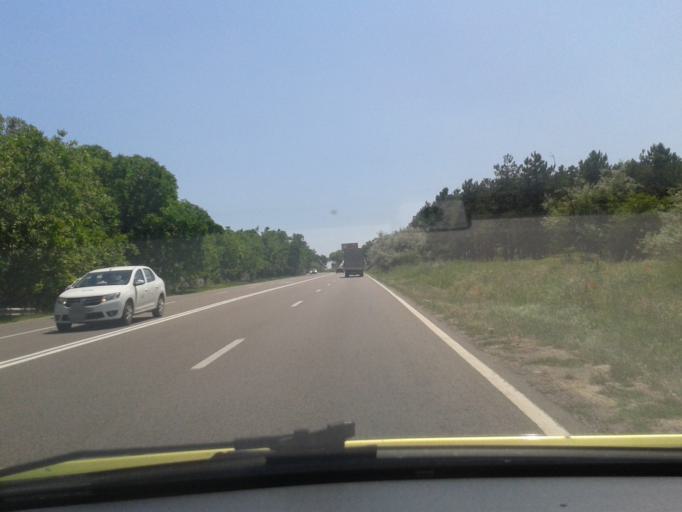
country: RO
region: Constanta
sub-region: Comuna Douazeci si Trei August
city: Douazeci si Trei August
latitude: 43.9012
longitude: 28.5709
